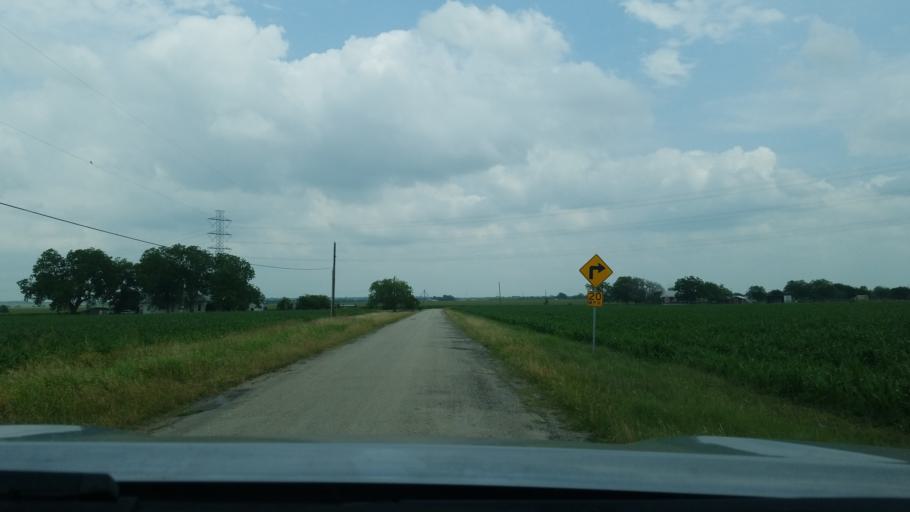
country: US
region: Texas
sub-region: Guadalupe County
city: Geronimo
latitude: 29.6787
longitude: -98.0174
